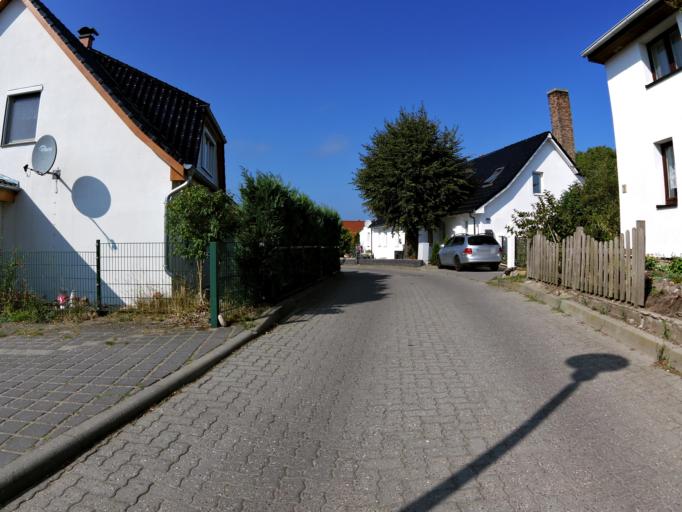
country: DE
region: Mecklenburg-Vorpommern
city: Loddin
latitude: 54.0125
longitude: 14.0432
